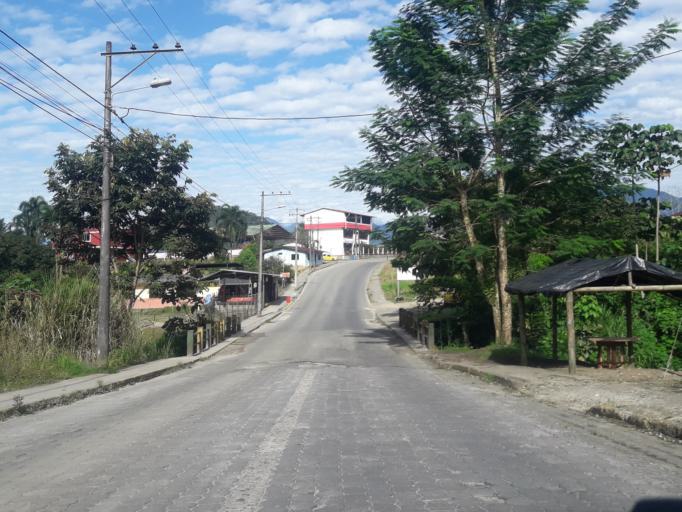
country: EC
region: Napo
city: Tena
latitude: -0.9862
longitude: -77.8256
